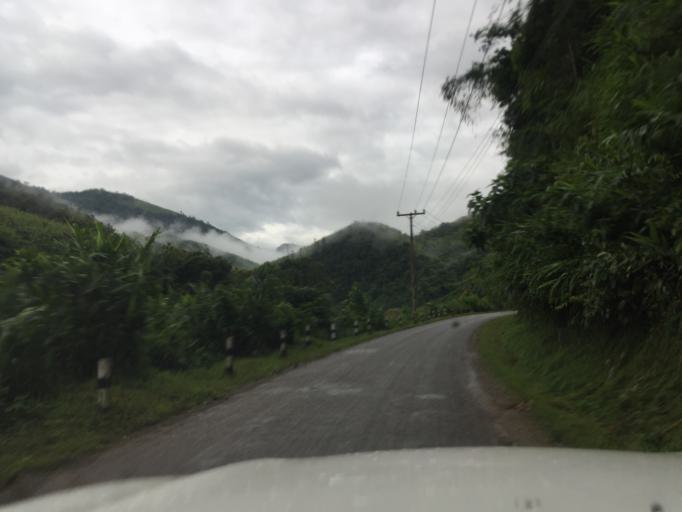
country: LA
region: Oudomxai
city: Muang La
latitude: 20.9258
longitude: 102.2047
